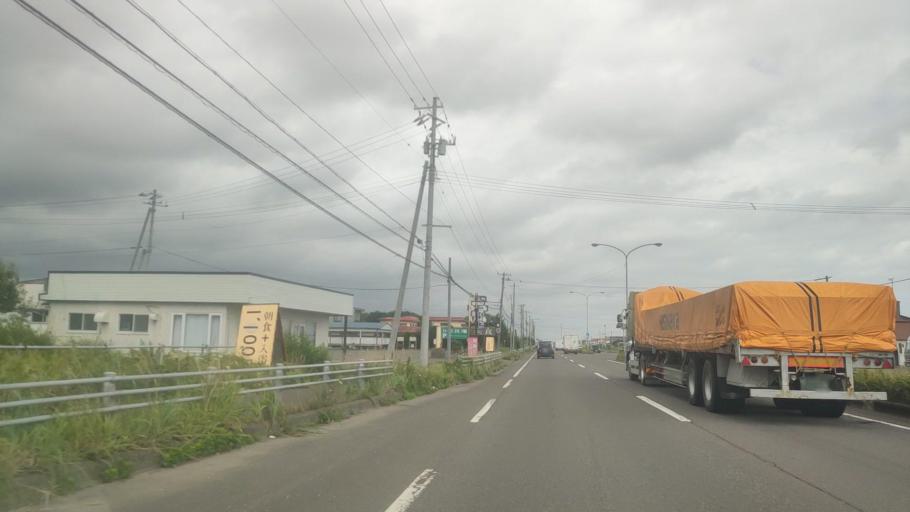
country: JP
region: Hokkaido
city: Shiraoi
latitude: 42.4726
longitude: 141.2336
